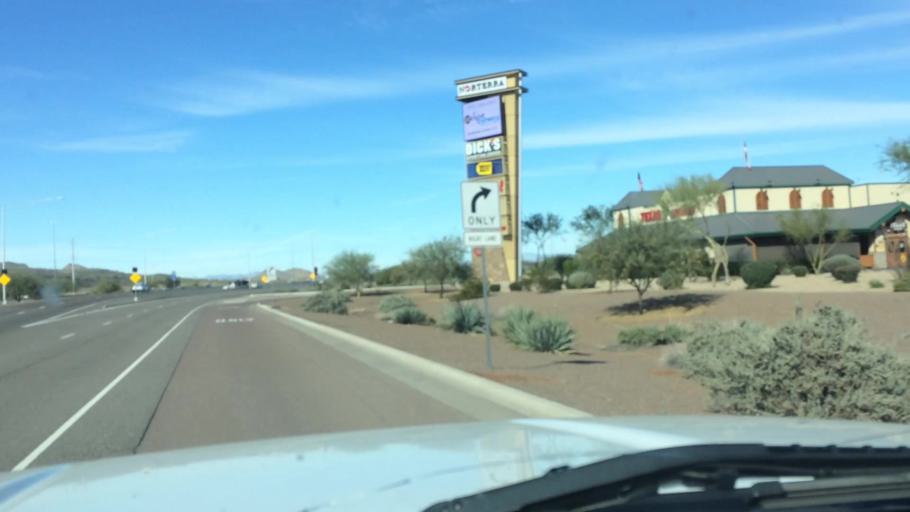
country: US
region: Arizona
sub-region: Maricopa County
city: Anthem
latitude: 33.7142
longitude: -112.1156
